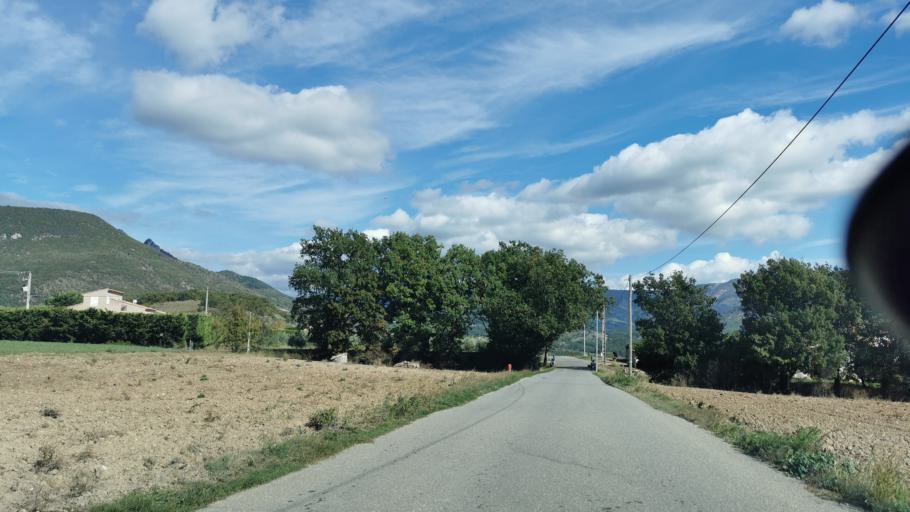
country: FR
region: Provence-Alpes-Cote d'Azur
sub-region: Departement des Alpes-de-Haute-Provence
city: Sisteron
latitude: 44.1796
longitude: 5.9803
